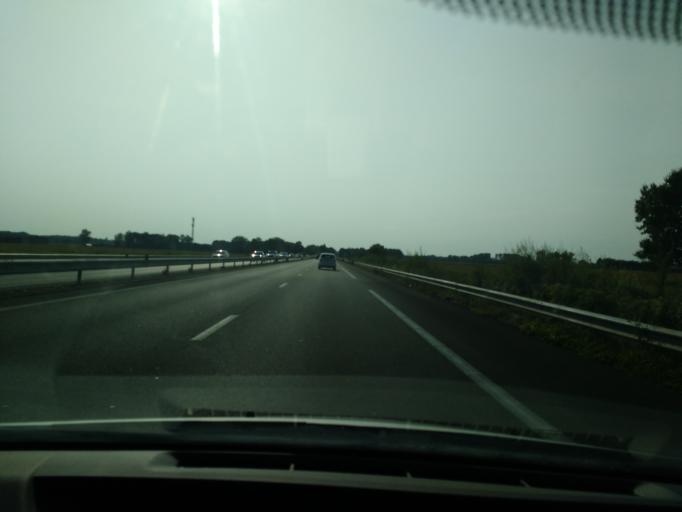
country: FR
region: Pays de la Loire
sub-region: Departement de Maine-et-Loire
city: Le Plessis-Grammoire
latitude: 47.5173
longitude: -0.3953
